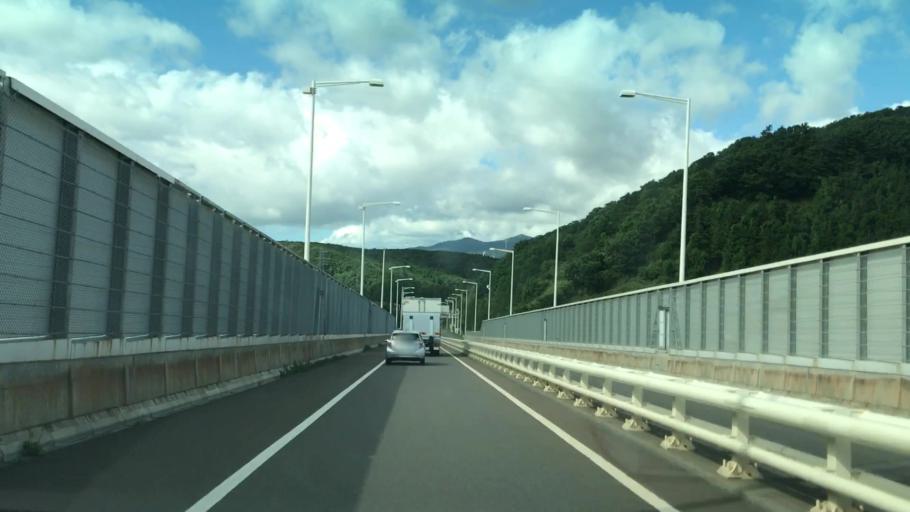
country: JP
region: Hokkaido
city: Muroran
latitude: 42.3611
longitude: 140.9515
